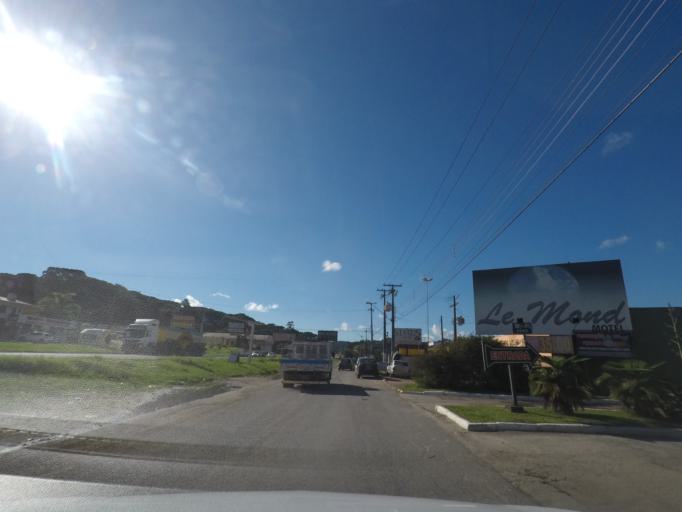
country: BR
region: Parana
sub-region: Almirante Tamandare
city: Almirante Tamandare
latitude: -25.3442
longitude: -49.2831
